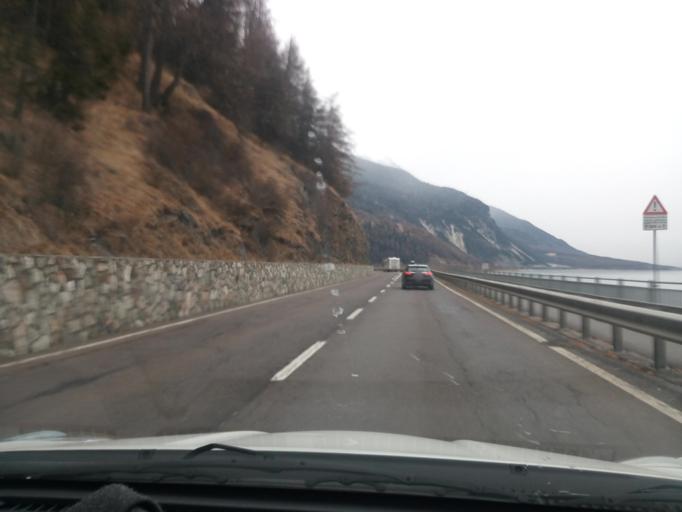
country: IT
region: Trentino-Alto Adige
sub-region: Bolzano
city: Curon Venosta
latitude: 46.8159
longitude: 10.5319
